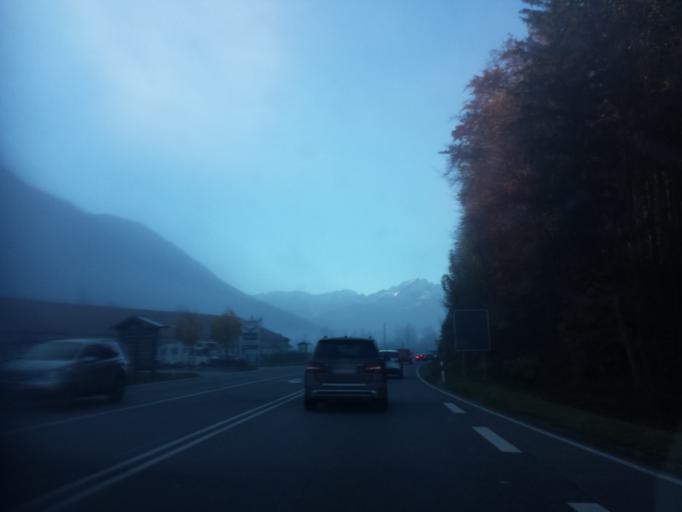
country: DE
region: Bavaria
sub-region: Upper Bavaria
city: Oberau
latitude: 47.5559
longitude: 11.1371
